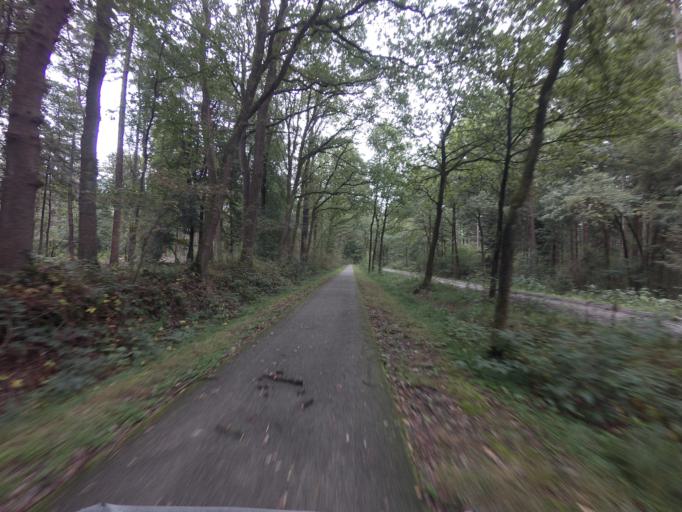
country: NL
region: Drenthe
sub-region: Gemeente Tynaarlo
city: Vries
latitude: 53.0777
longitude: 6.4659
